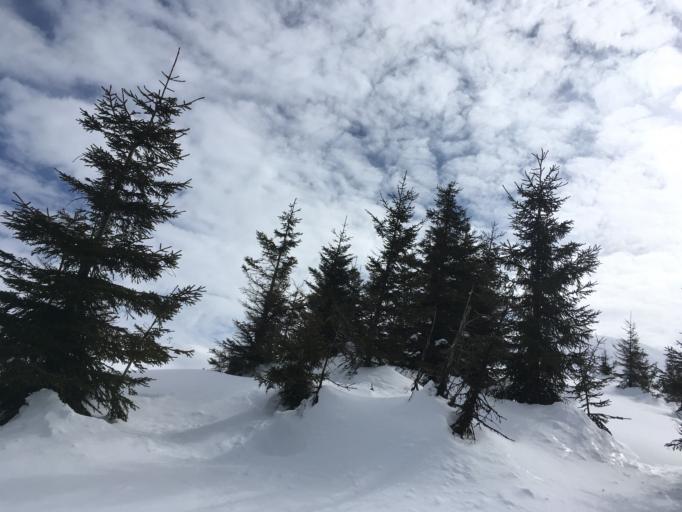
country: GE
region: Ajaria
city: Dioknisi
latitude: 41.6225
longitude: 42.4950
